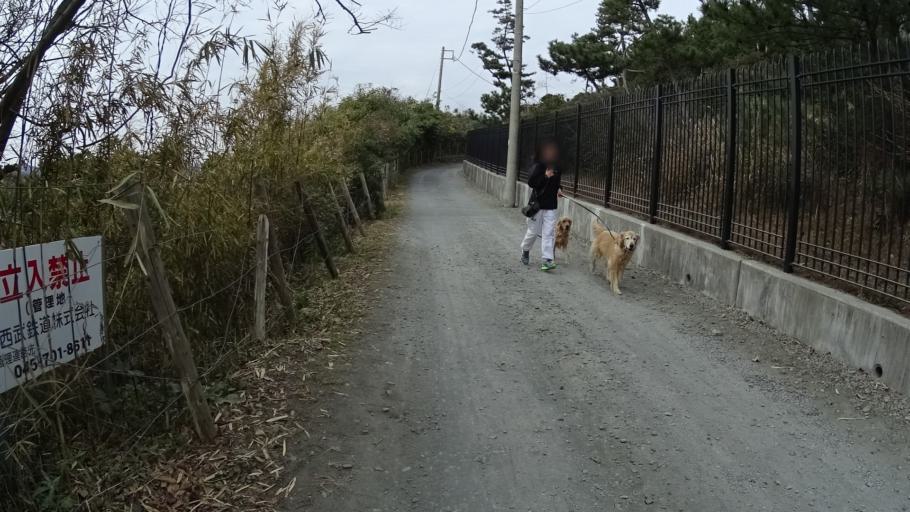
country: JP
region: Kanagawa
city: Oiso
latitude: 35.3022
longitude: 139.2894
